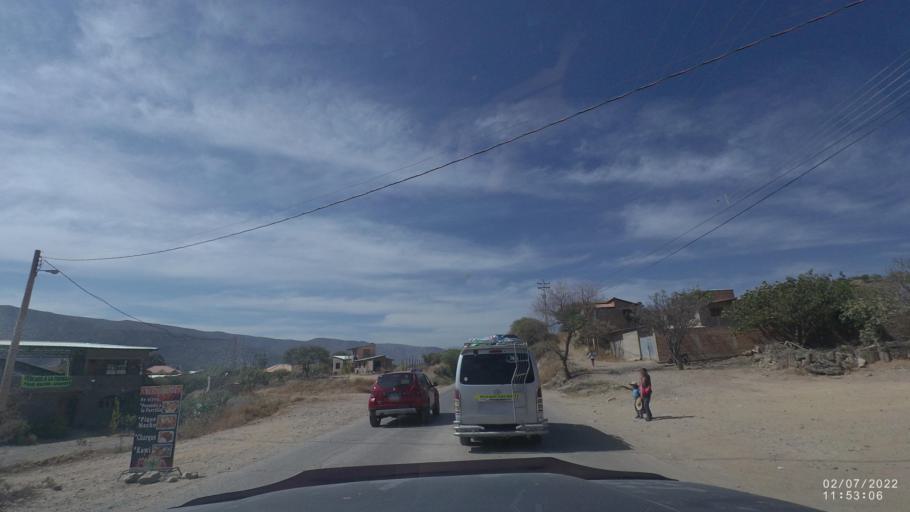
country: BO
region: Cochabamba
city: Sipe Sipe
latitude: -17.5824
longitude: -66.3316
